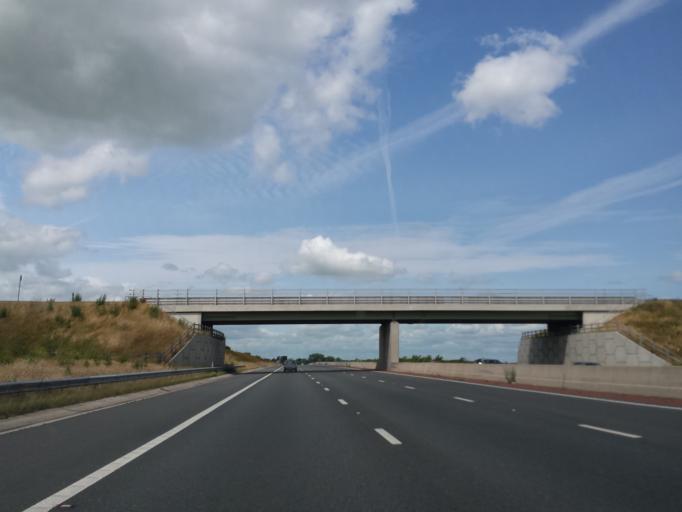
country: GB
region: England
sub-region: North Yorkshire
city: Ripon
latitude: 54.2384
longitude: -1.4983
